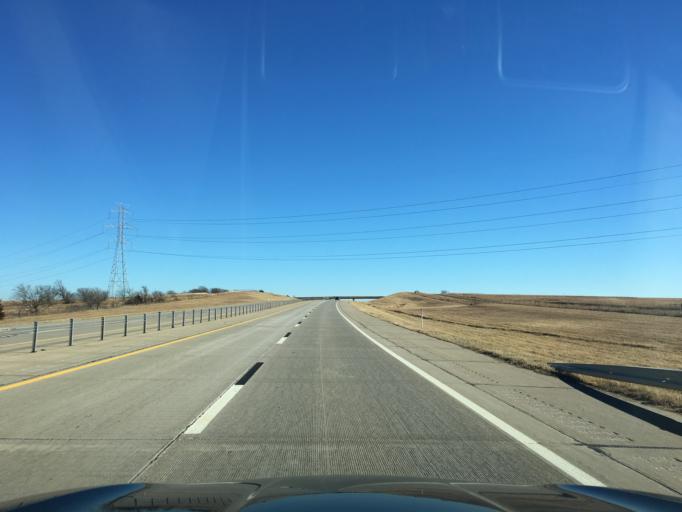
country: US
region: Oklahoma
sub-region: Noble County
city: Perry
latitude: 36.3921
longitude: -97.1099
